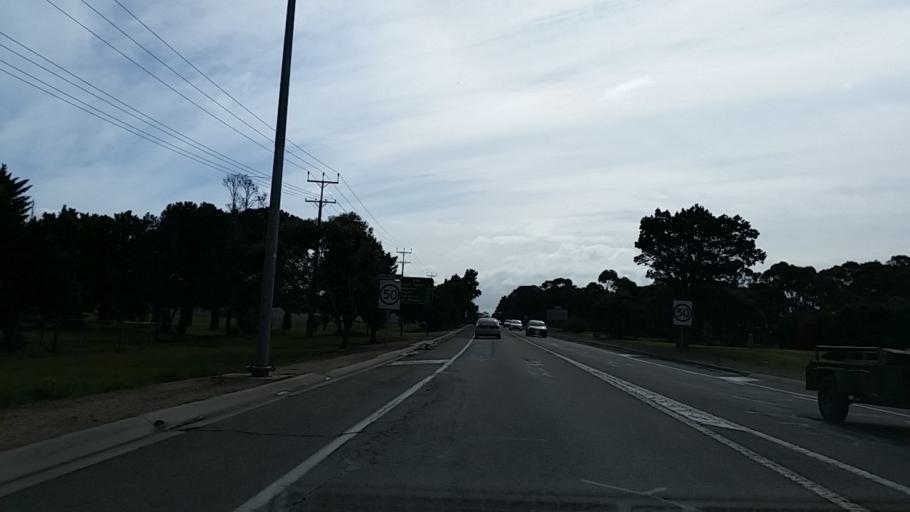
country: AU
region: South Australia
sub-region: Murray Bridge
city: Murray Bridge
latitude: -35.1477
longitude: 139.2861
